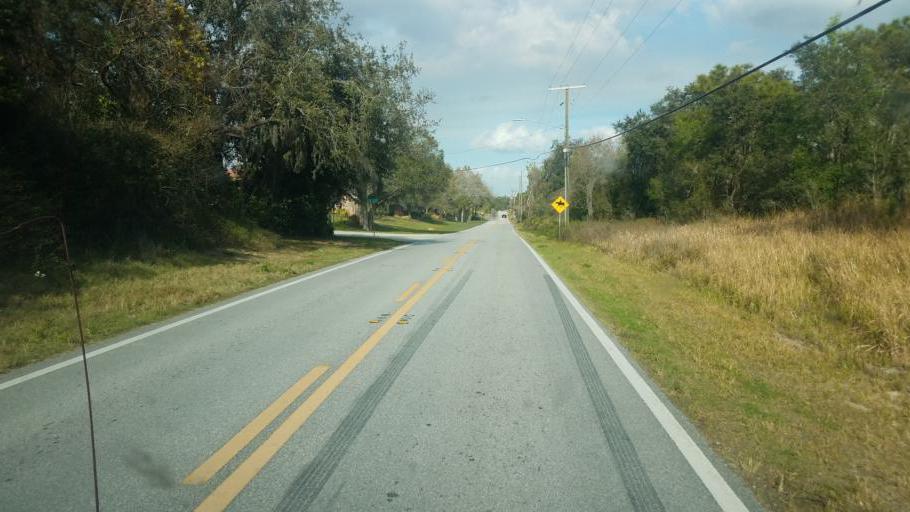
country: US
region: Florida
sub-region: Polk County
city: Loughman
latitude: 28.2306
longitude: -81.5786
